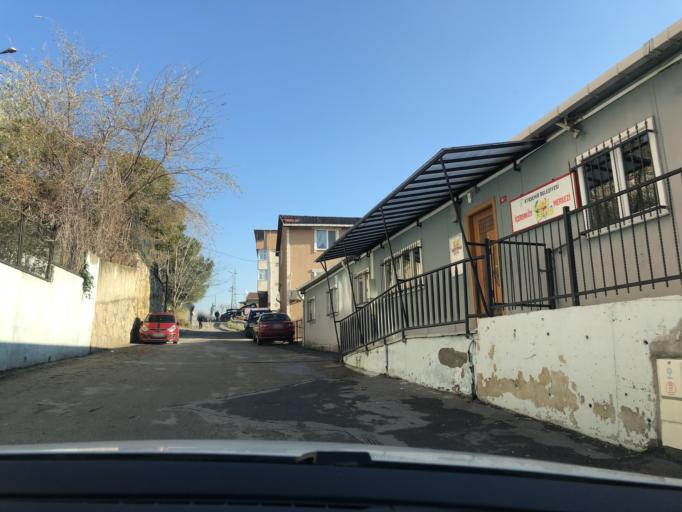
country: TR
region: Istanbul
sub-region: Atasehir
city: Atasehir
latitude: 40.9677
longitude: 29.1207
